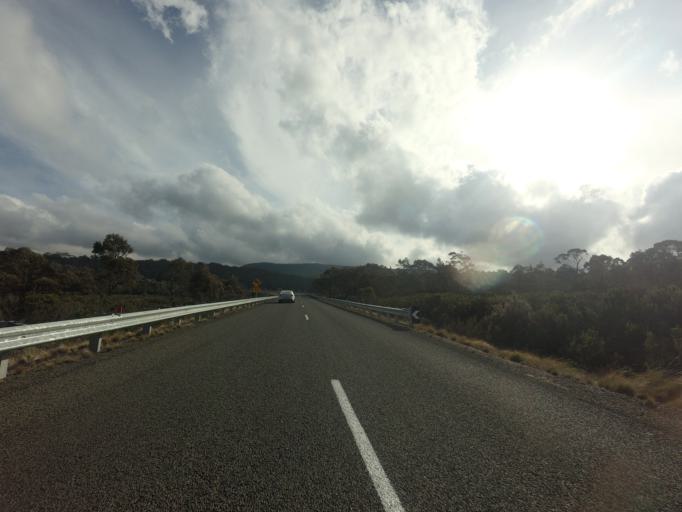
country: AU
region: Tasmania
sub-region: Meander Valley
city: Deloraine
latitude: -41.7864
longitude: 146.6968
